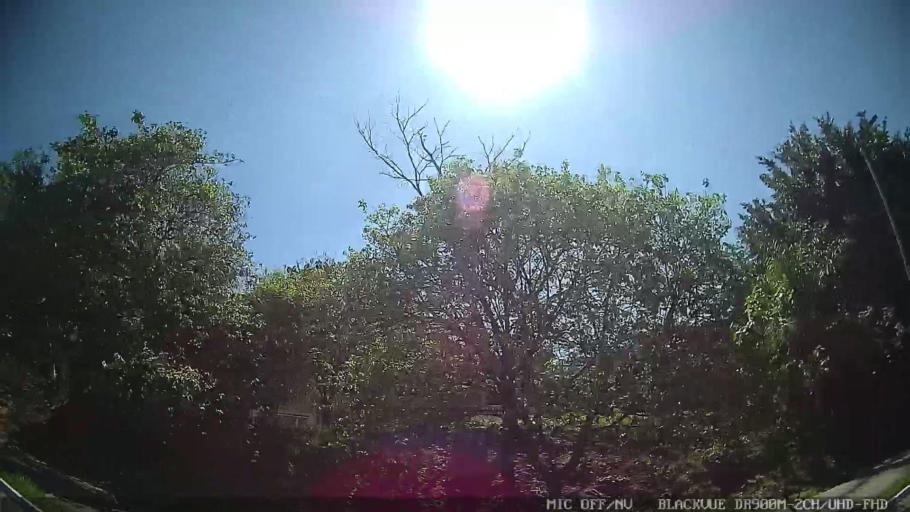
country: BR
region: Sao Paulo
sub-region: Sao Caetano Do Sul
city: Sao Caetano do Sul
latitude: -23.5925
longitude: -46.5069
